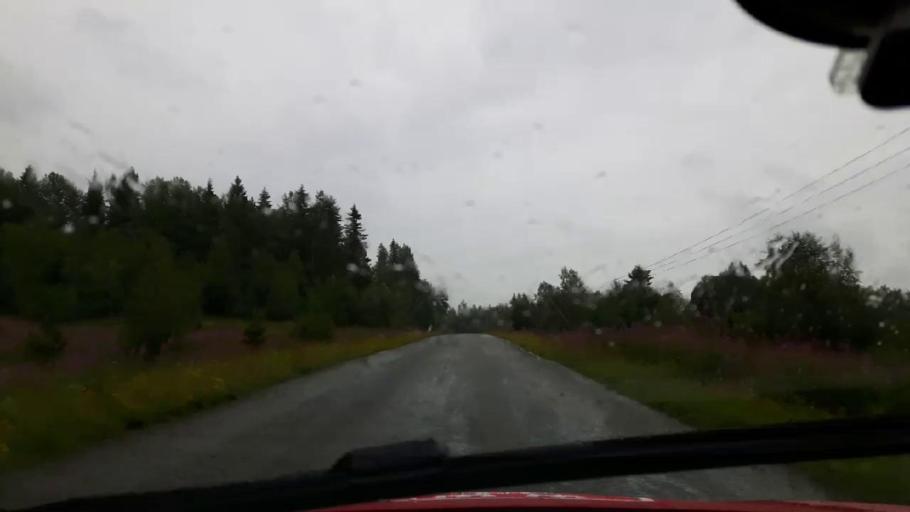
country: SE
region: Jaemtland
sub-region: OEstersunds Kommun
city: Brunflo
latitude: 62.8562
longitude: 14.9572
